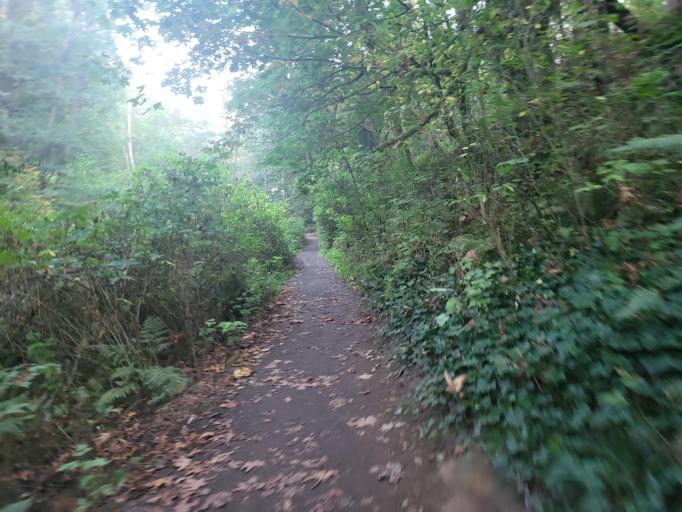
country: US
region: Washington
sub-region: Pierce County
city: Tacoma
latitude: 47.3162
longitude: -122.4143
